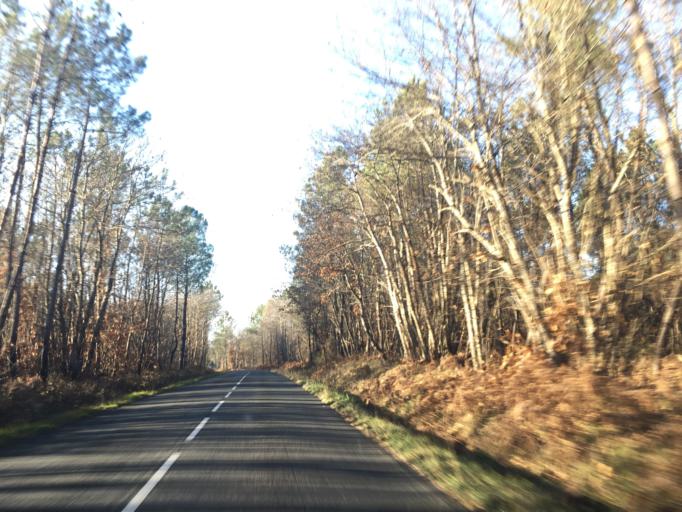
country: FR
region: Aquitaine
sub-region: Departement de la Dordogne
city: Neuvic
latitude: 45.1555
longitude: 0.4153
